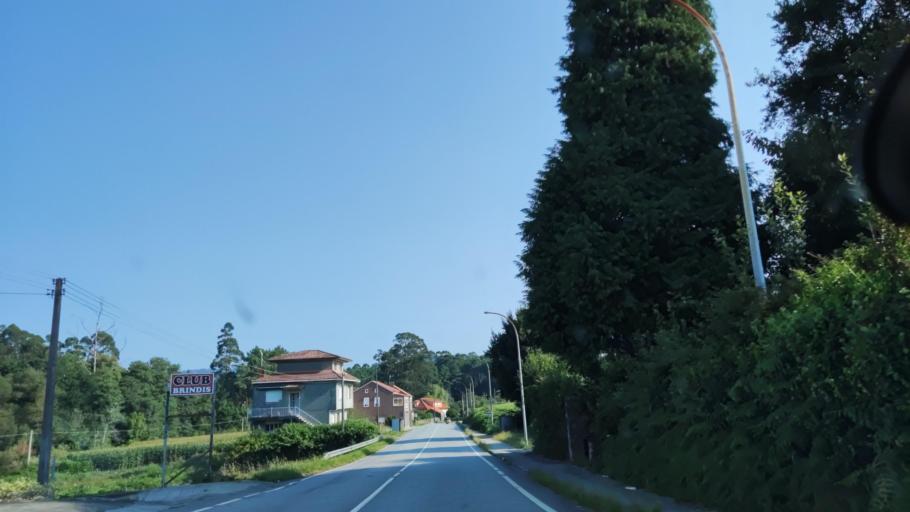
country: ES
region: Galicia
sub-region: Provincia da Coruna
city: Rianxo
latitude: 42.6807
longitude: -8.8524
